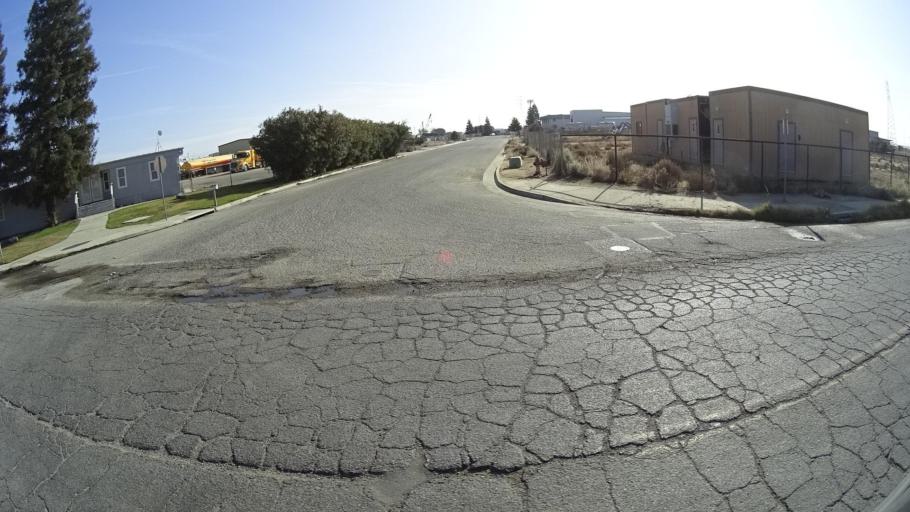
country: US
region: California
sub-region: Kern County
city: Oildale
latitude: 35.4539
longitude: -119.0368
